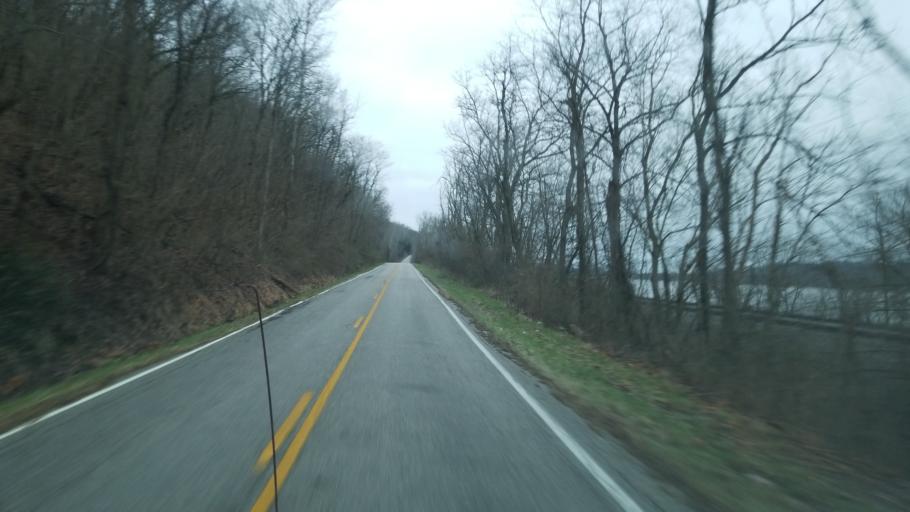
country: US
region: Kentucky
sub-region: Bracken County
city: Augusta
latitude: 38.7664
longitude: -84.0428
